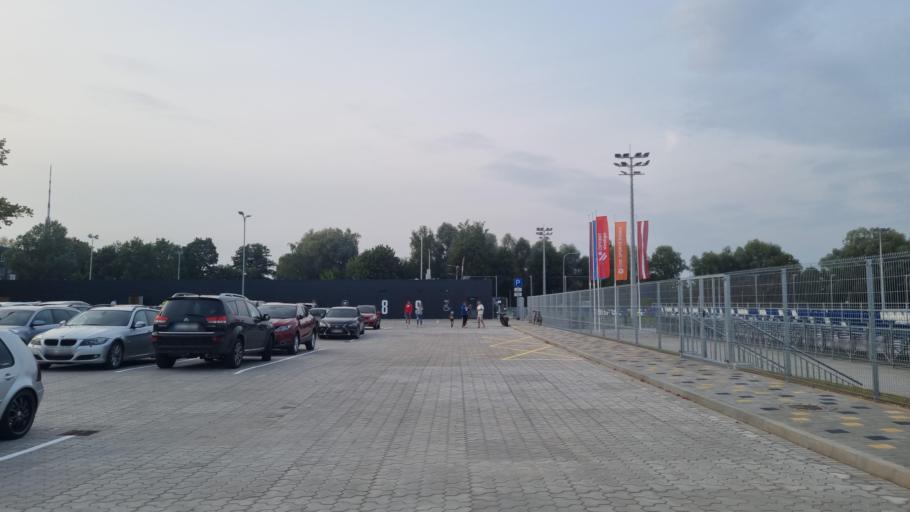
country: LV
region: Kekava
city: Balozi
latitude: 56.9079
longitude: 24.1542
